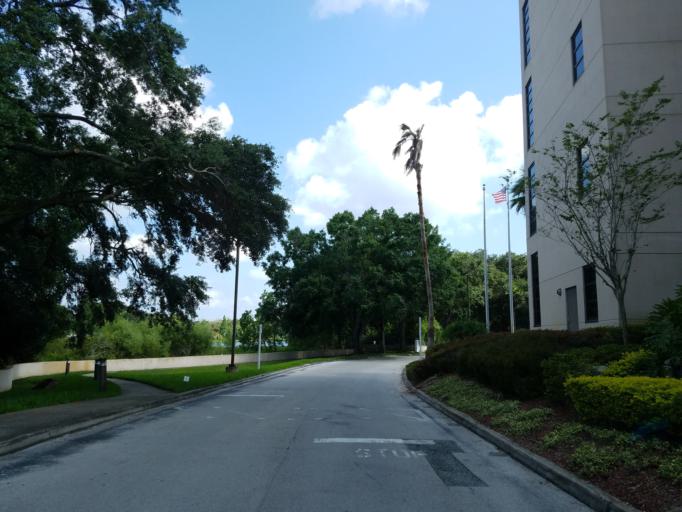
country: US
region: Florida
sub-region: Hillsborough County
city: Brandon
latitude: 27.9324
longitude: -82.2869
